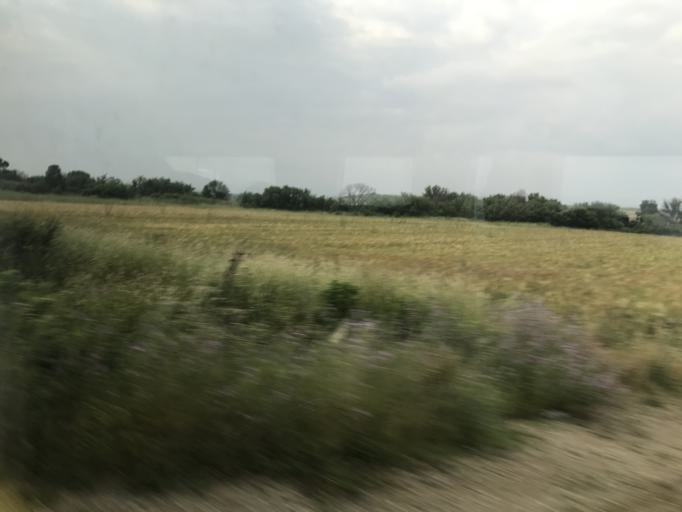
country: GR
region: East Macedonia and Thrace
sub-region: Nomos Rodopis
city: Lykeio
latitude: 41.0451
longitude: 25.6383
